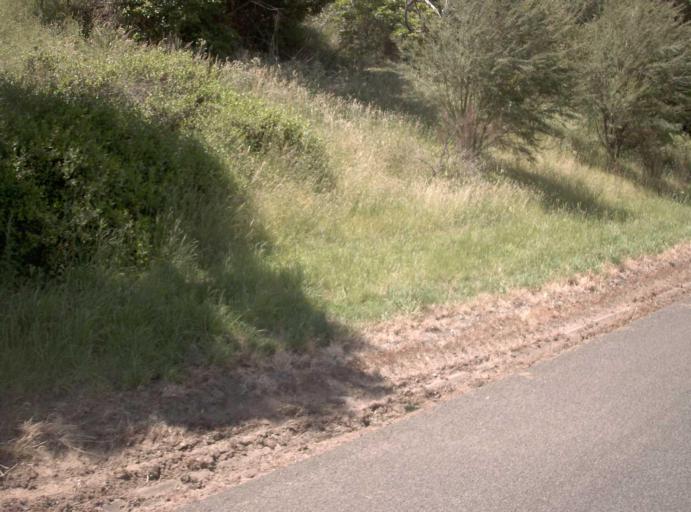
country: AU
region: Victoria
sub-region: Baw Baw
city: Warragul
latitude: -38.1188
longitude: 145.8675
